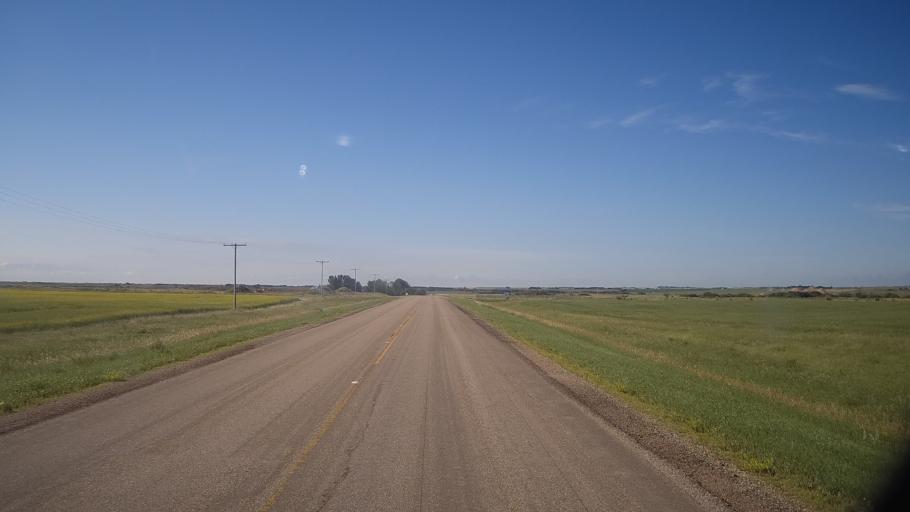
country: CA
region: Saskatchewan
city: Watrous
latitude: 51.7262
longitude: -105.3574
